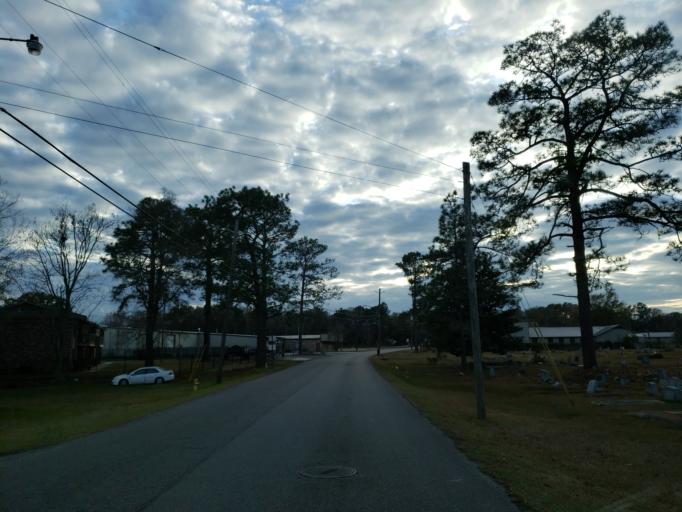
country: US
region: Mississippi
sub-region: Forrest County
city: Hattiesburg
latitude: 31.3048
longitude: -89.3107
